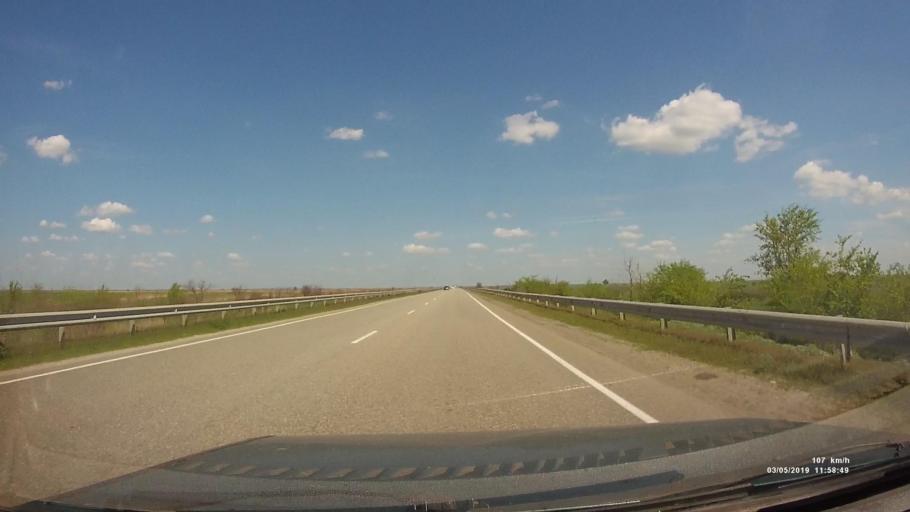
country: RU
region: Rostov
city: Bagayevskaya
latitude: 47.2261
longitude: 40.3239
